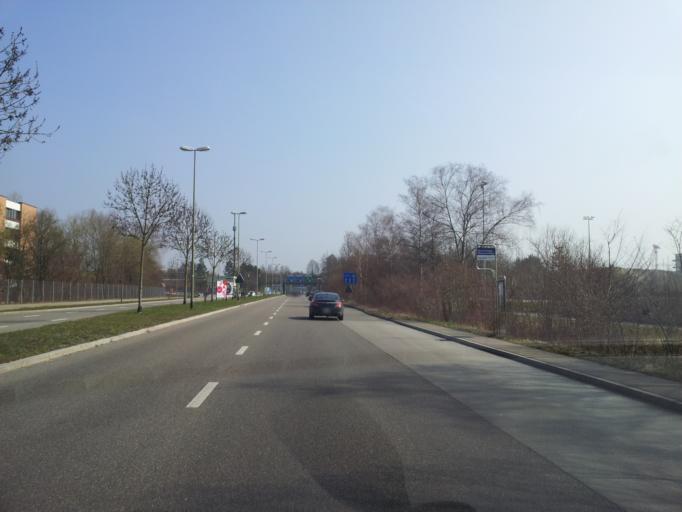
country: CH
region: Zurich
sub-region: Bezirk Zuerich
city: Zuerich (Kreis 12) / Hirzenbach
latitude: 47.4045
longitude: 8.5953
